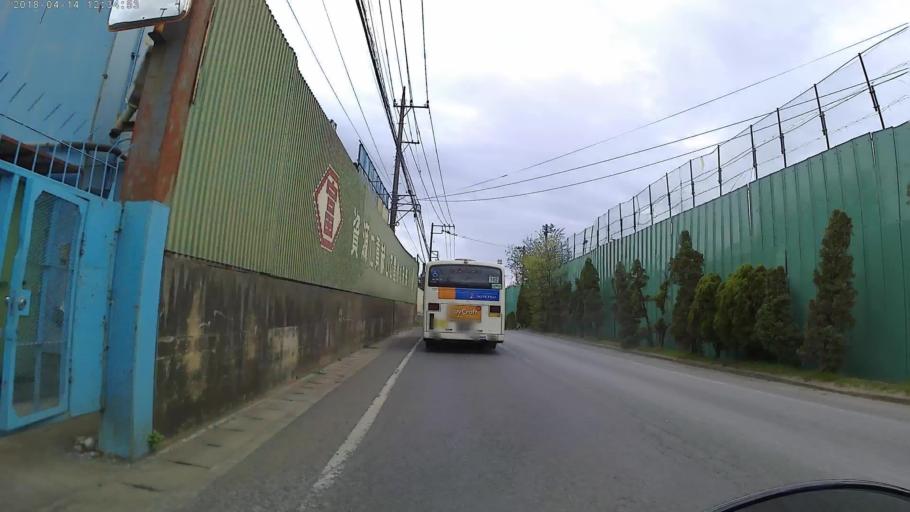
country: JP
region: Kanagawa
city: Atsugi
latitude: 35.4237
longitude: 139.4092
